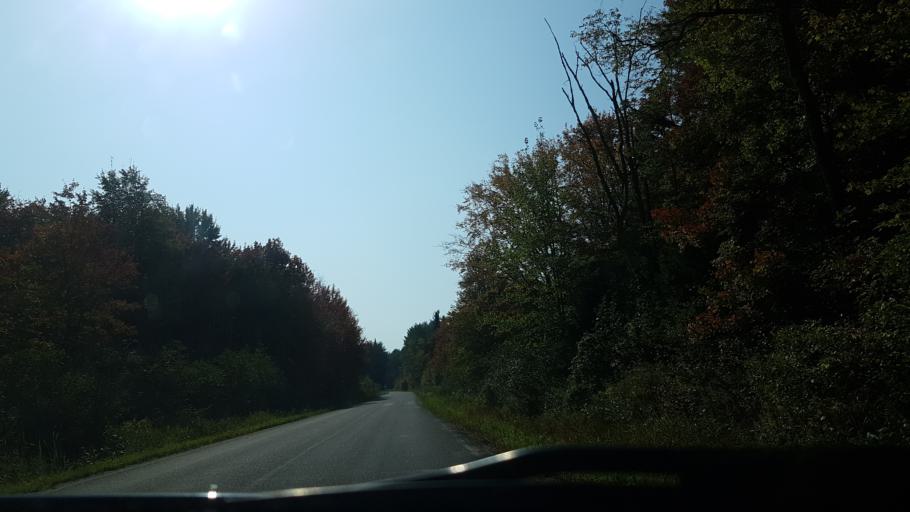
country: CA
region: Ontario
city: Bracebridge
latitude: 44.9698
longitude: -79.2565
